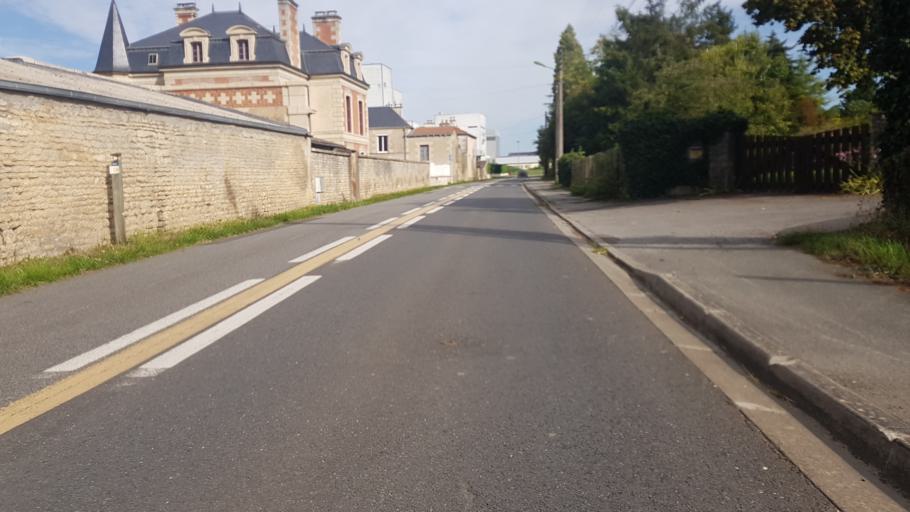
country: FR
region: Poitou-Charentes
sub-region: Departement de la Vienne
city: Chasseneuil-du-Poitou
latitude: 46.6227
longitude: 0.3623
